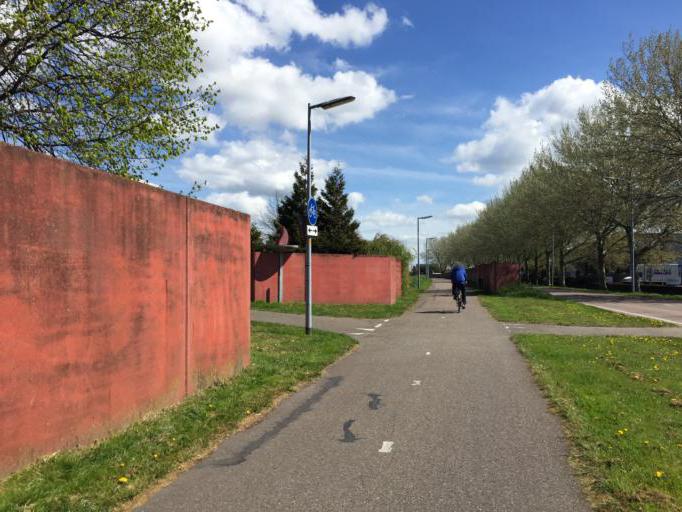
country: NL
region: South Holland
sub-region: Gemeente Lisse
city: Lisse
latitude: 52.2544
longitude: 4.5737
